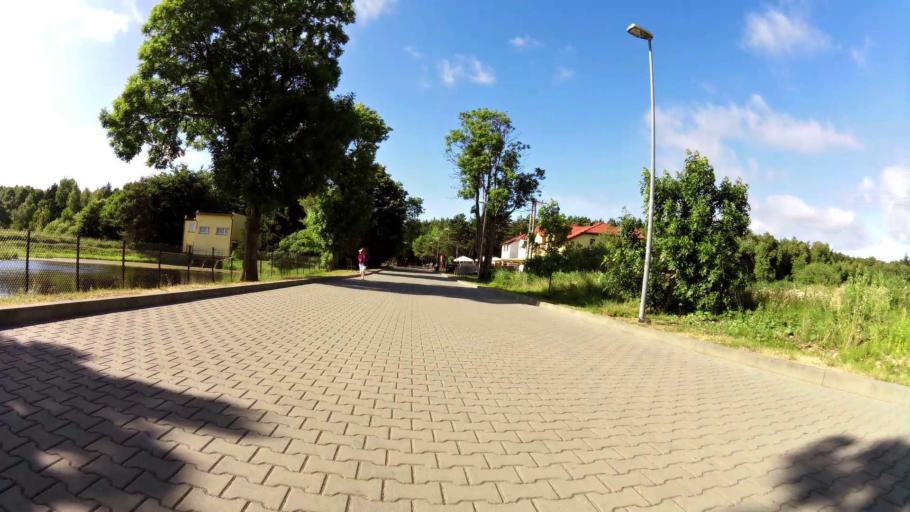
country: PL
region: West Pomeranian Voivodeship
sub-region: Powiat kolobrzeski
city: Grzybowo
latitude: 54.1642
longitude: 15.4841
